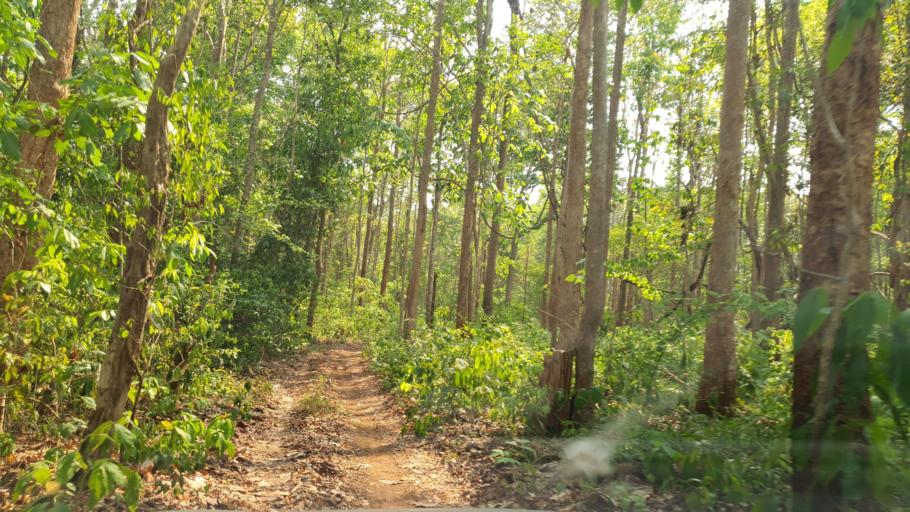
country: TH
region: Chiang Mai
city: San Sai
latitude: 19.0019
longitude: 99.1222
